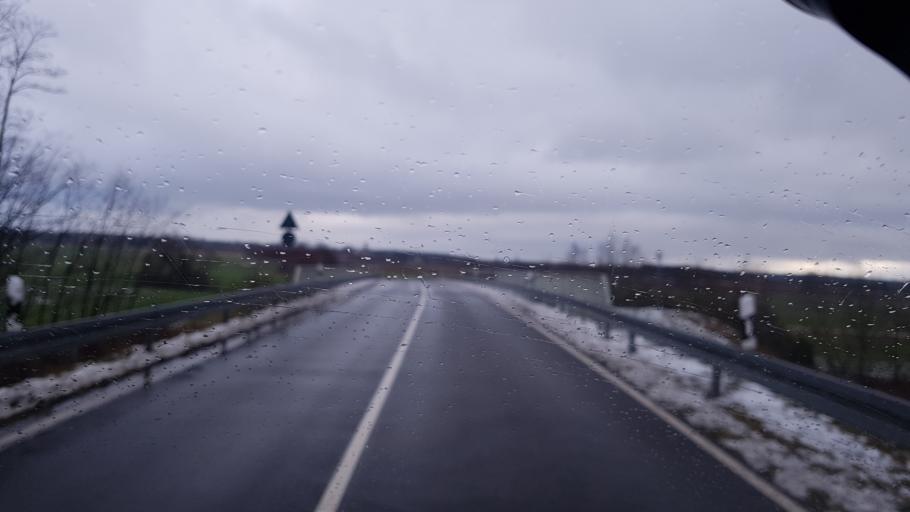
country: DE
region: Brandenburg
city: Schenkendobern
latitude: 51.8944
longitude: 14.6378
